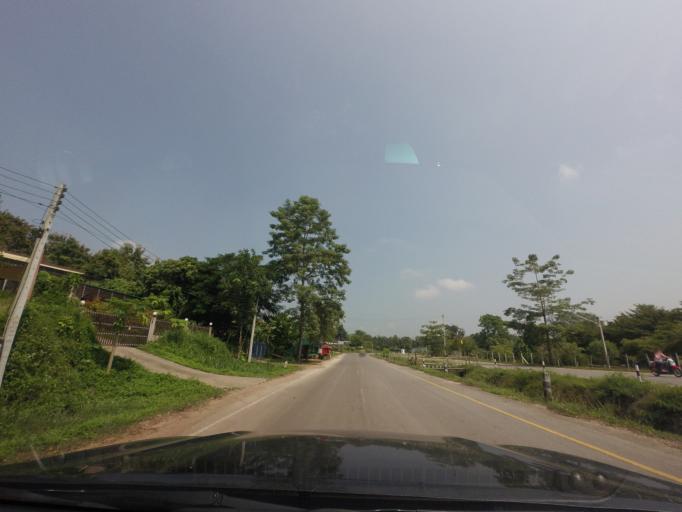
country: TH
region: Nan
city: Nan
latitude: 18.7945
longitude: 100.7555
